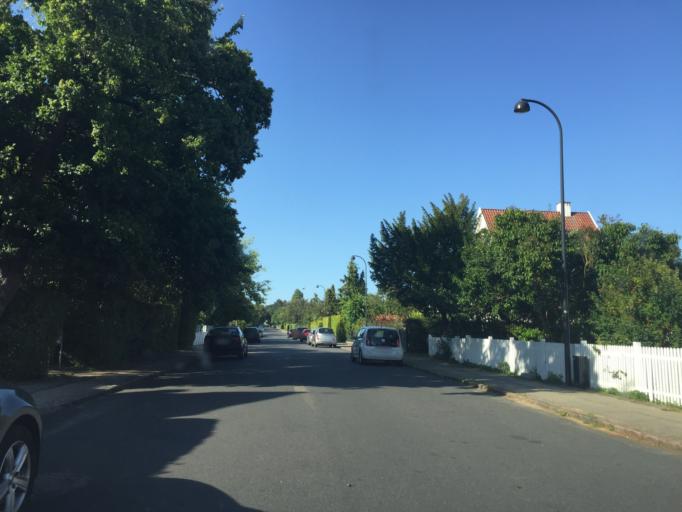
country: DK
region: Capital Region
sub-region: Gentofte Kommune
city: Charlottenlund
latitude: 55.7614
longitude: 12.5568
